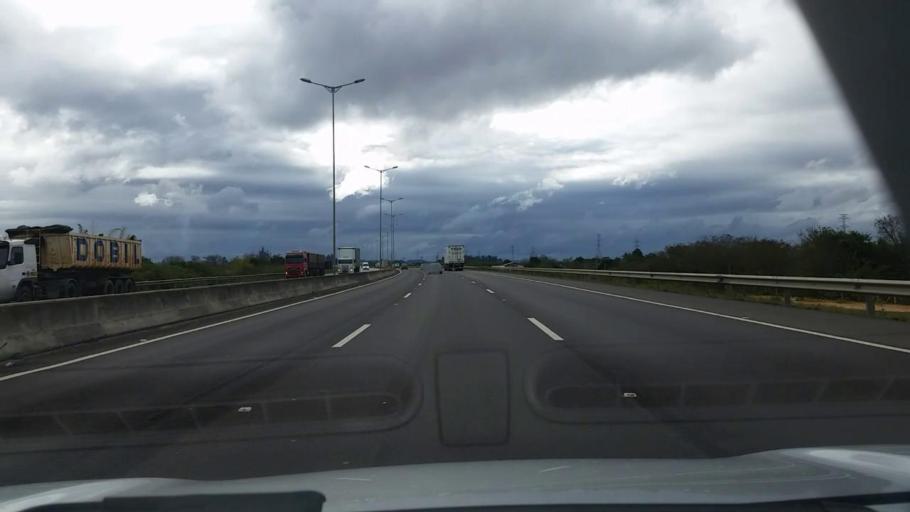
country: BR
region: Rio Grande do Sul
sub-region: Canoas
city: Canoas
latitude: -29.9386
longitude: -51.2066
